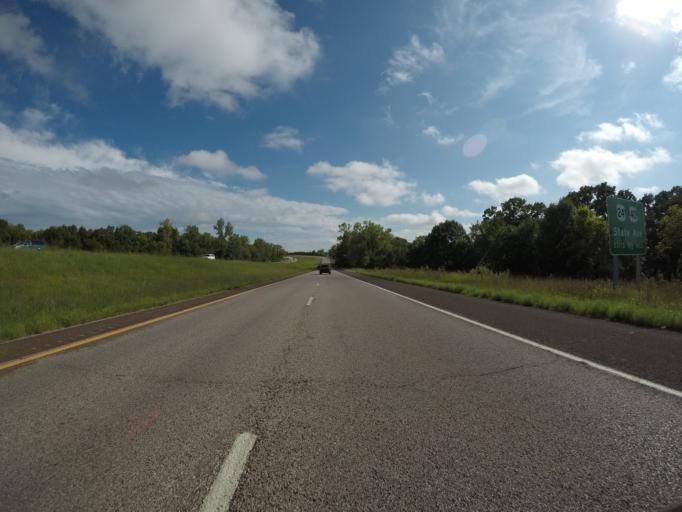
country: US
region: Kansas
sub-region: Leavenworth County
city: Basehor
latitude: 39.1270
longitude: -94.9015
